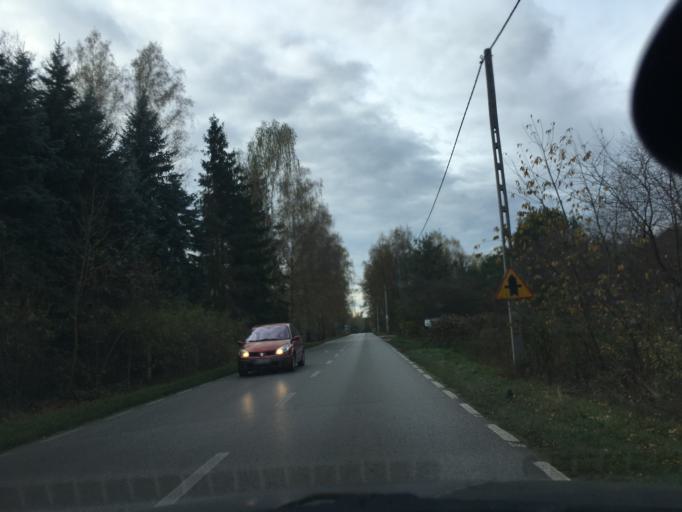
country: PL
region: Masovian Voivodeship
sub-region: Powiat piaseczynski
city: Prazmow
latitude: 51.9860
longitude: 20.9214
